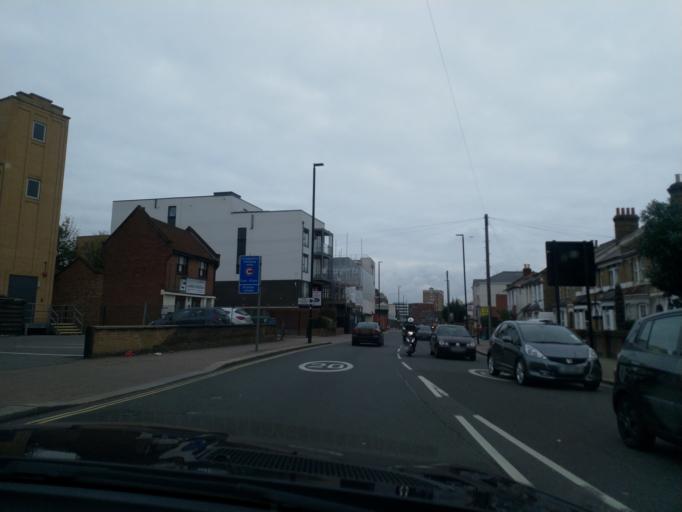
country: GB
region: England
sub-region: Greater London
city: Hounslow
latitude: 51.4682
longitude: -0.3612
